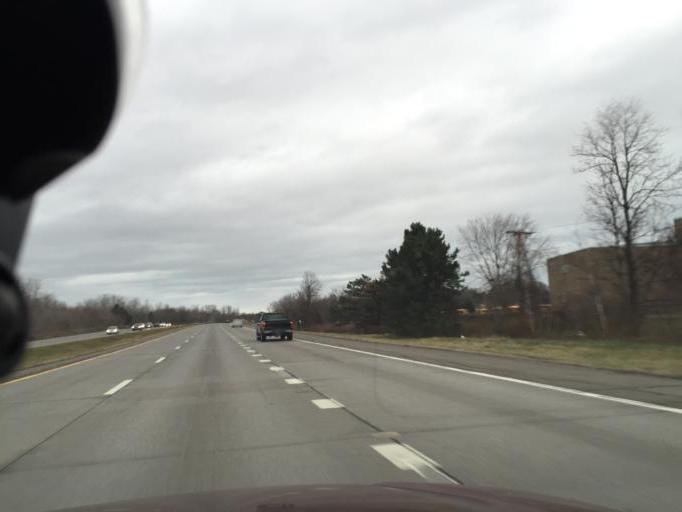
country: US
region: New York
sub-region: Monroe County
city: Greece
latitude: 43.2209
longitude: -77.6747
